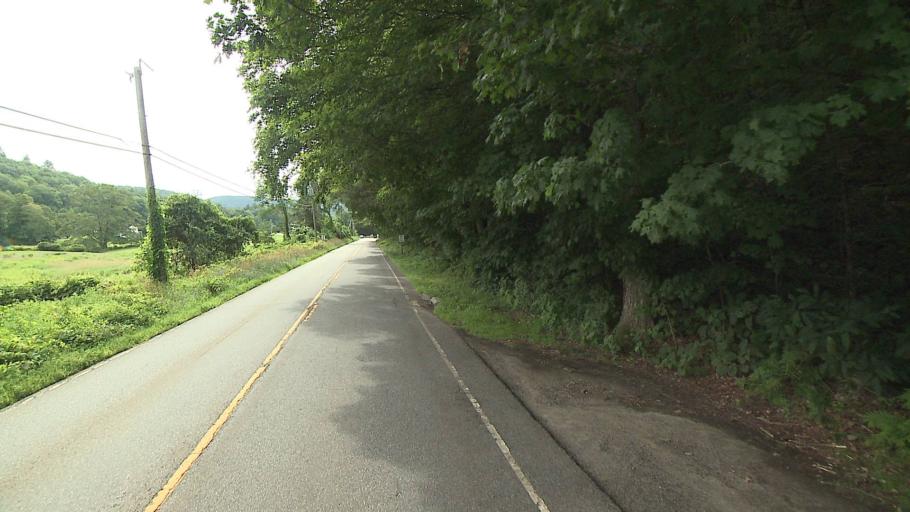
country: US
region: Connecticut
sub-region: Litchfield County
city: Kent
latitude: 41.7310
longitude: -73.4906
